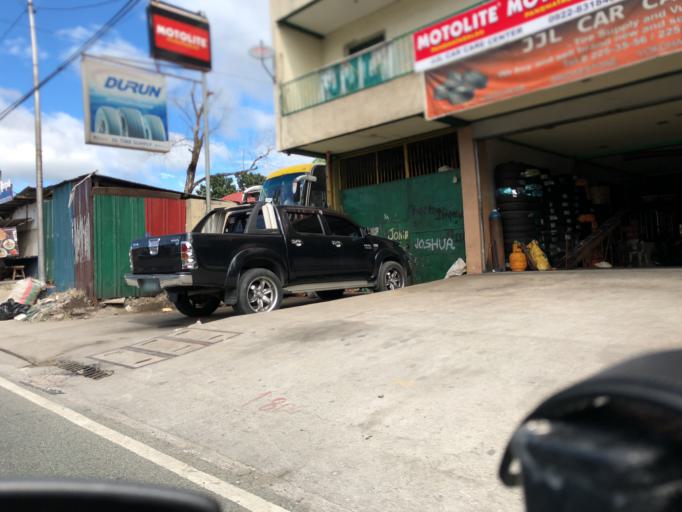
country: PH
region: Calabarzon
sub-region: Province of Rizal
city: San Mateo
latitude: 14.7254
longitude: 121.0612
